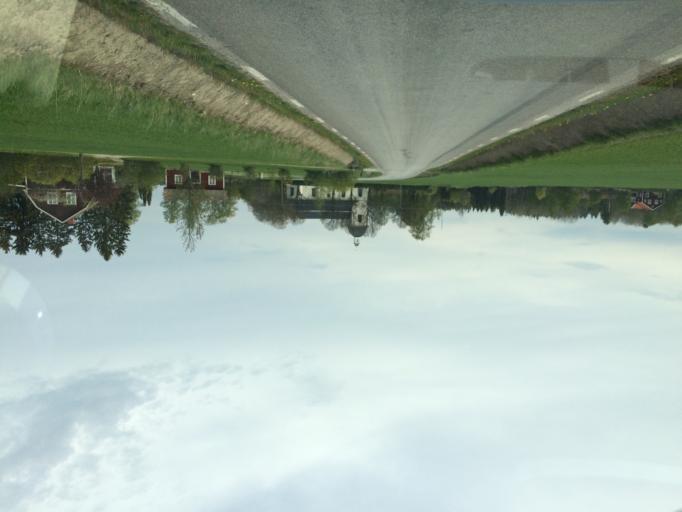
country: SE
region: Vaestmanland
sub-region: Kopings Kommun
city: Koping
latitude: 59.5812
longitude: 15.9866
